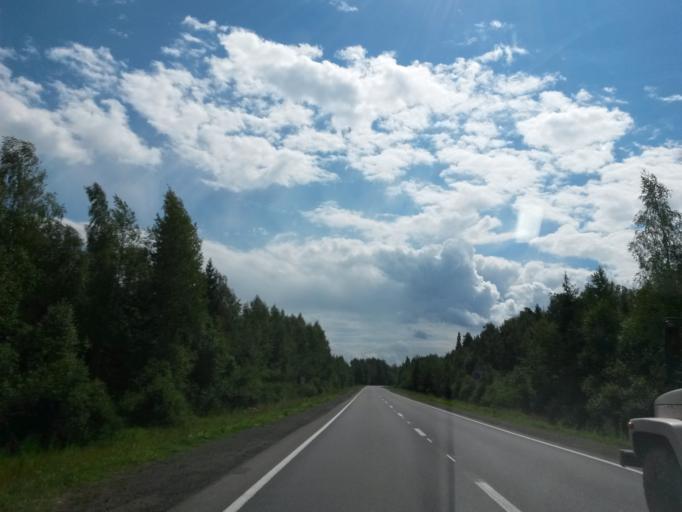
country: RU
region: Jaroslavl
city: Gavrilov-Yam
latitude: 57.2909
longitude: 39.9509
